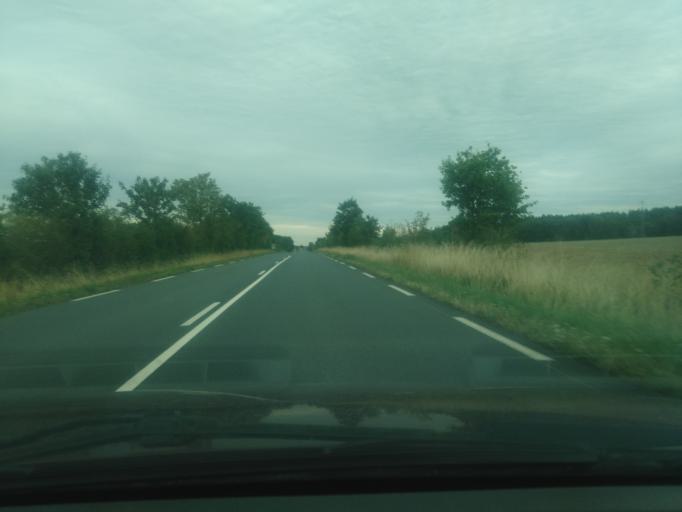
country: FR
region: Centre
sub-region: Departement de l'Indre
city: Arthon
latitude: 46.6113
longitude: 1.6665
